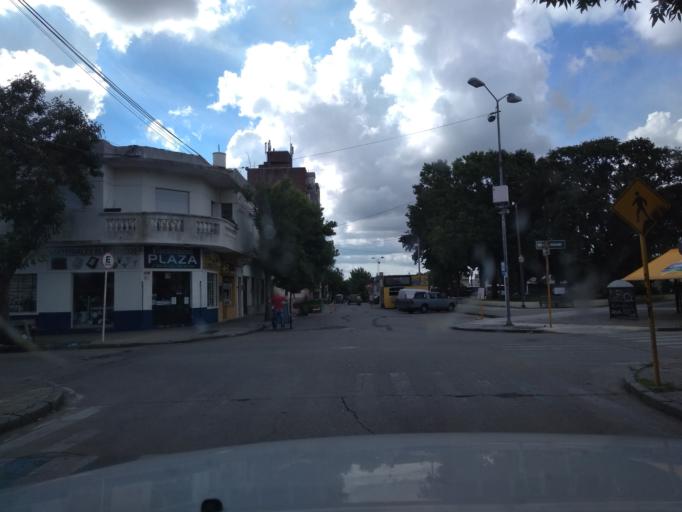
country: UY
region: Florida
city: Florida
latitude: -34.0946
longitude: -56.2185
